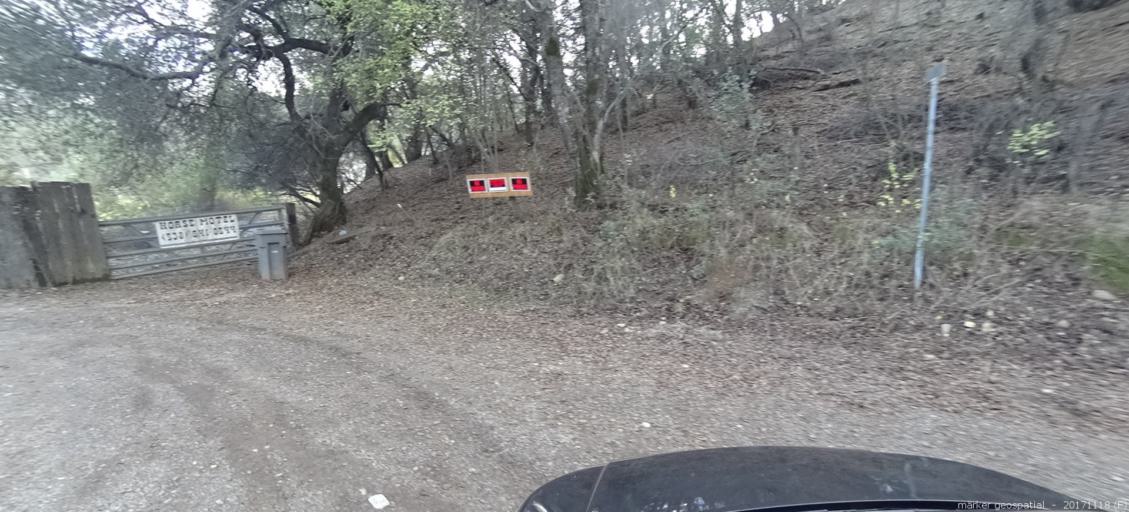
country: US
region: California
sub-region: Shasta County
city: Anderson
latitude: 40.4512
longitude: -122.3248
